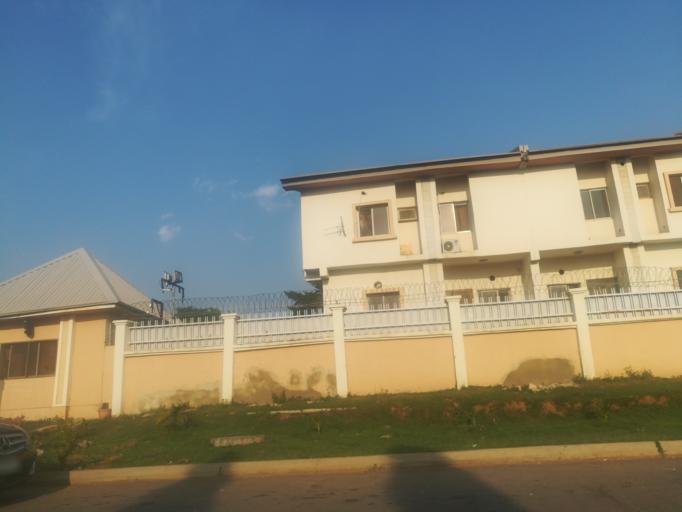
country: NG
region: Abuja Federal Capital Territory
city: Abuja
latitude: 9.0520
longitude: 7.4514
